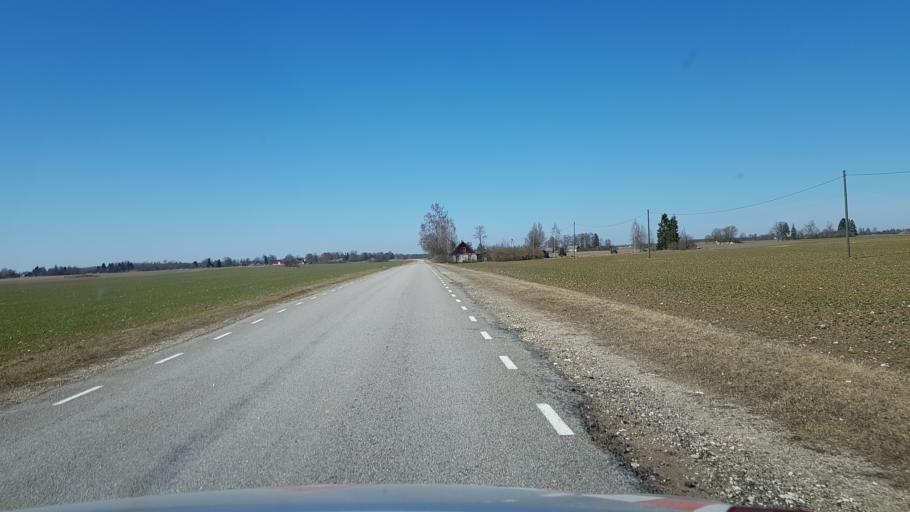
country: EE
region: Laeaene-Virumaa
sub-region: Vaeike-Maarja vald
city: Vaike-Maarja
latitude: 59.0993
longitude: 26.3967
